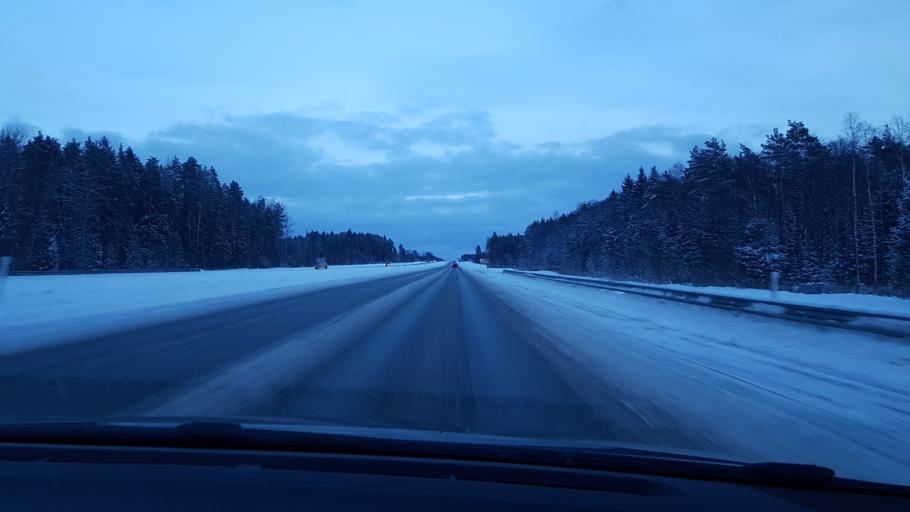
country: EE
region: Harju
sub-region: Raasiku vald
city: Raasiku
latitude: 59.4381
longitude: 25.2506
